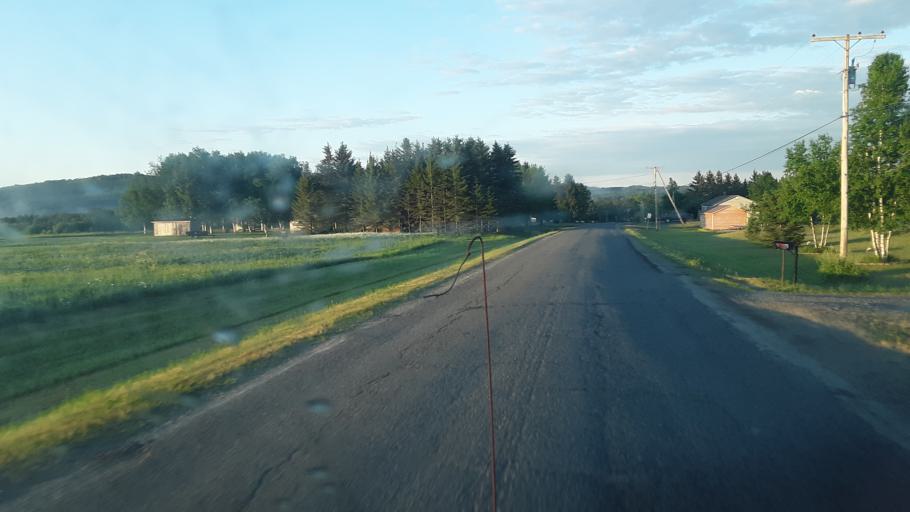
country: US
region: Maine
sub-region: Aroostook County
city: Presque Isle
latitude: 46.7598
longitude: -68.1021
